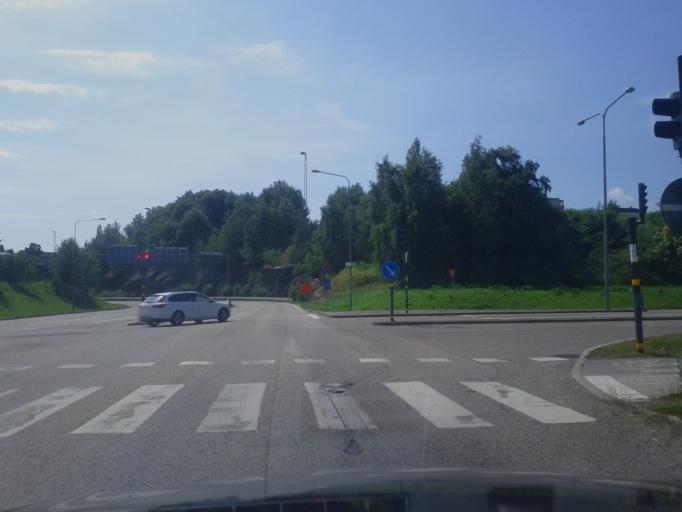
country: SE
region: Stockholm
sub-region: Stockholms Kommun
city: Arsta
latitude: 59.2866
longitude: 18.0456
